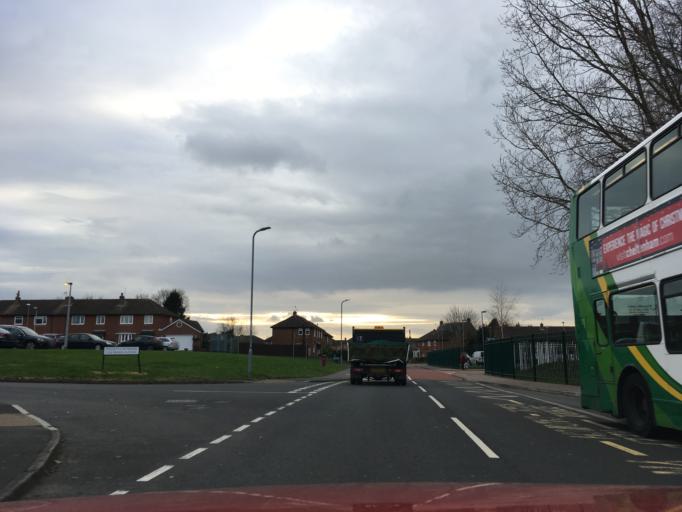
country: GB
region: Wales
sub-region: Monmouthshire
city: Caldicot
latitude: 51.5924
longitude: -2.7578
